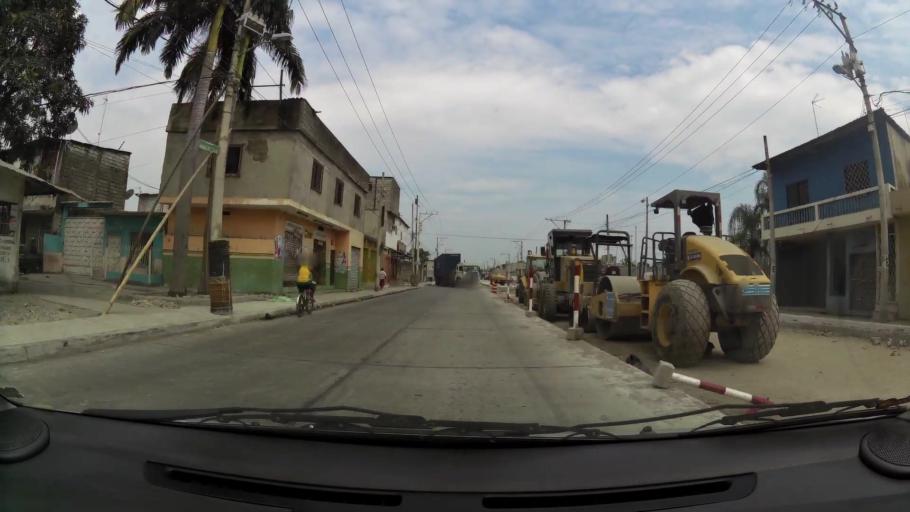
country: EC
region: Guayas
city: Guayaquil
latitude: -2.2454
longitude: -79.9256
